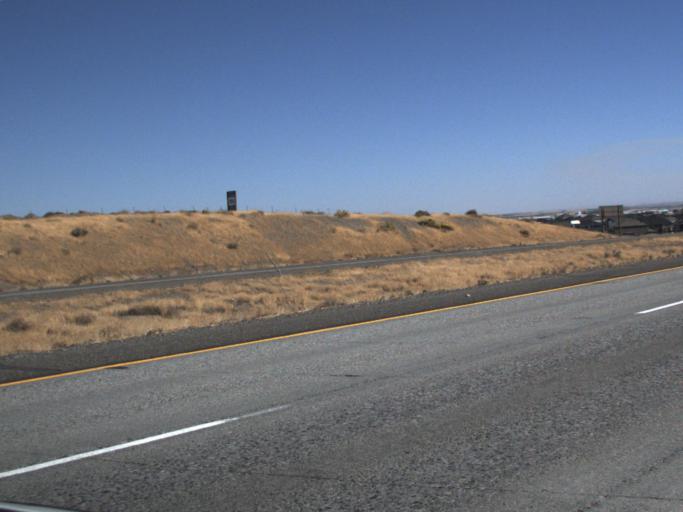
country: US
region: Washington
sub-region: Franklin County
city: West Pasco
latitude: 46.2598
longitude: -119.1639
